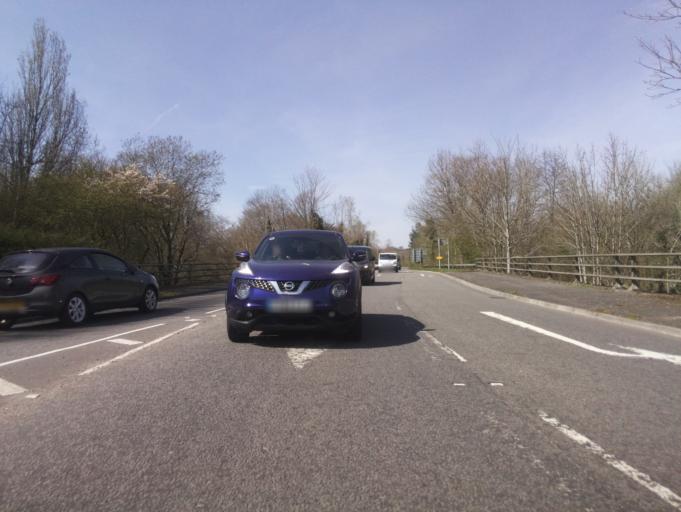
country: GB
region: Wales
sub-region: Rhondda Cynon Taf
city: Aberdare
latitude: 51.7221
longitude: -3.4525
